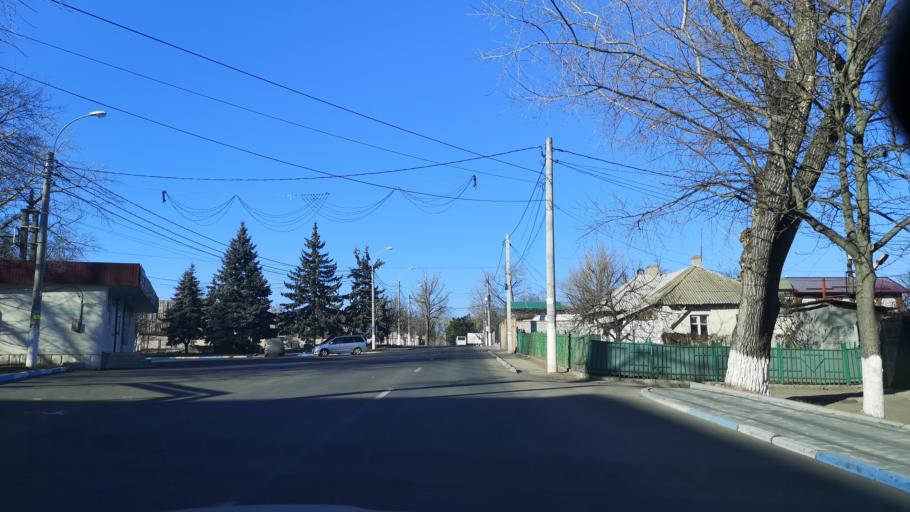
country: MD
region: Chisinau
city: Cricova
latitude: 47.1411
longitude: 28.8647
